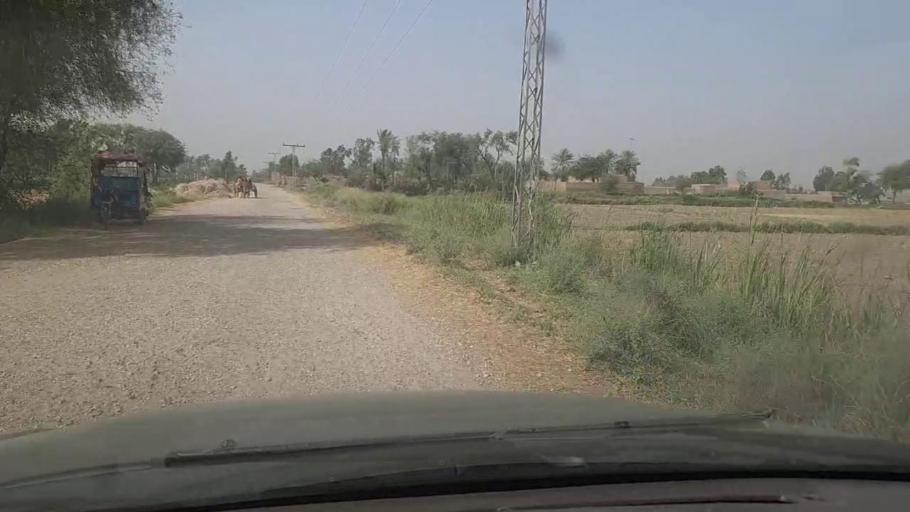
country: PK
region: Sindh
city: Garhi Yasin
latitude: 27.8745
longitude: 68.5616
